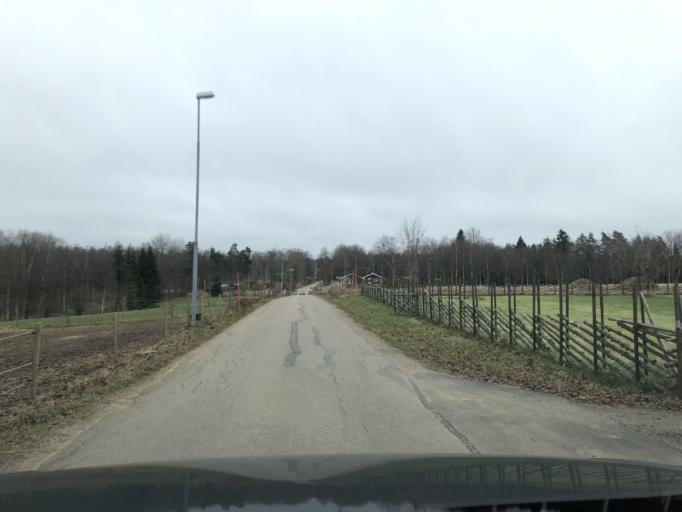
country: SE
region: Vaestra Goetaland
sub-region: Boras Kommun
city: Sjomarken
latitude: 57.7613
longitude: 12.8431
